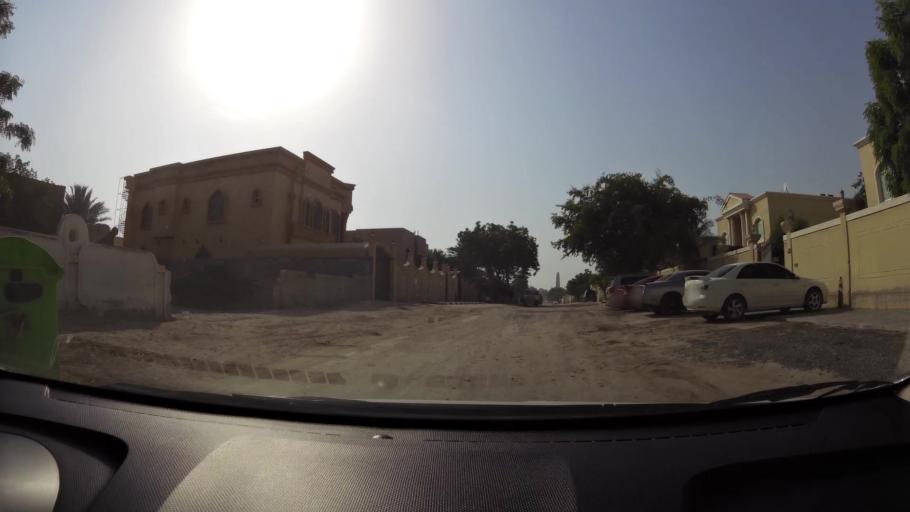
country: AE
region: Ajman
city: Ajman
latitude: 25.3785
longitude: 55.4223
